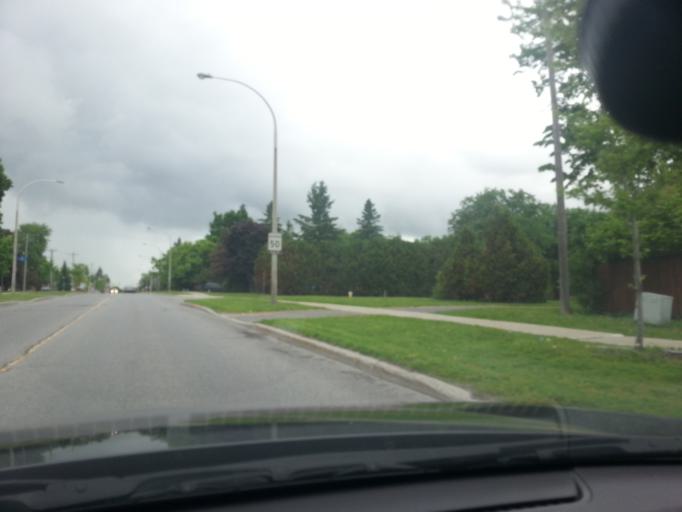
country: CA
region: Ontario
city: Bells Corners
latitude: 45.2524
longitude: -75.9134
